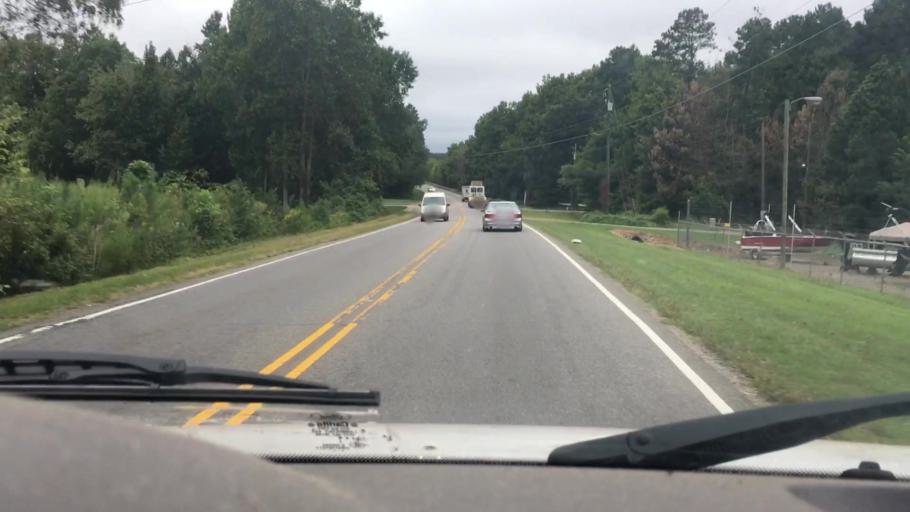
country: US
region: North Carolina
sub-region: Catawba County
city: Lake Norman of Catawba
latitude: 35.6061
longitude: -80.9350
